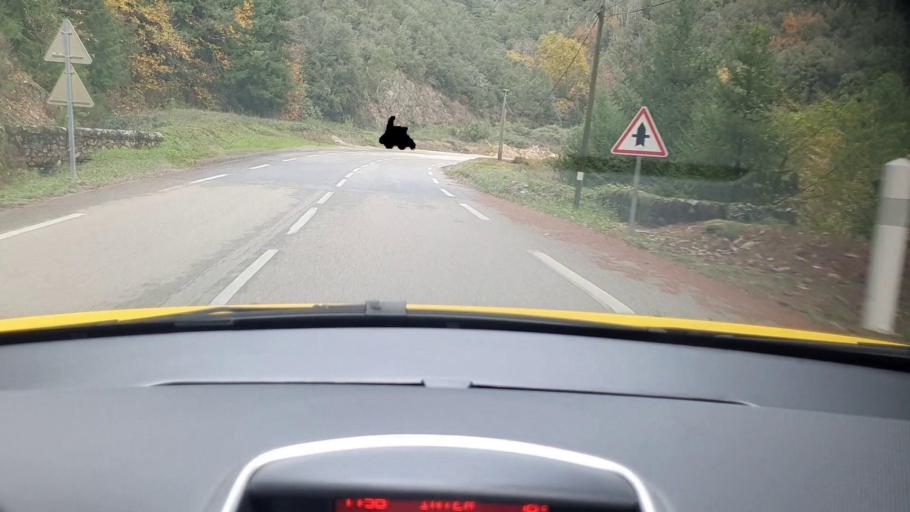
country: FR
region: Languedoc-Roussillon
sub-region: Departement du Gard
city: Saint-Jean-du-Gard
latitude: 44.1091
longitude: 3.8116
